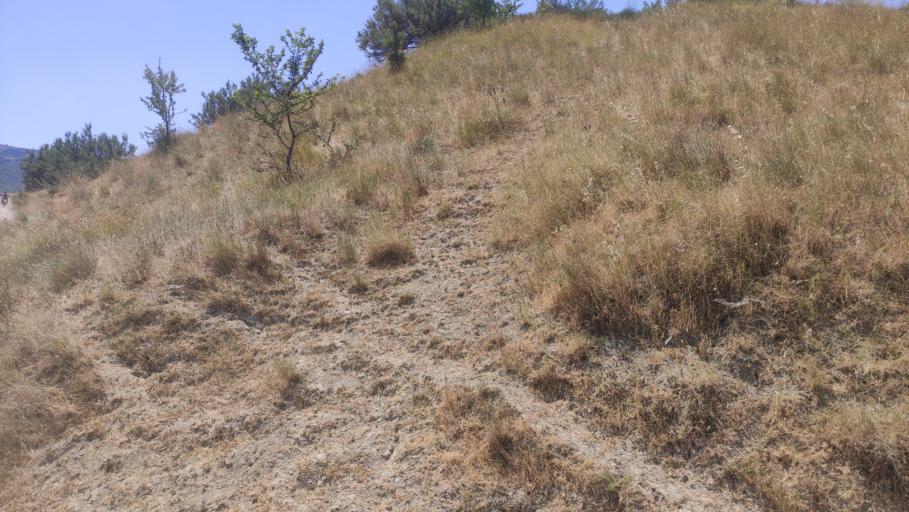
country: IT
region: Abruzzo
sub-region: Provincia di Pescara
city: Serramonacesca
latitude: 42.2628
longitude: 14.1009
